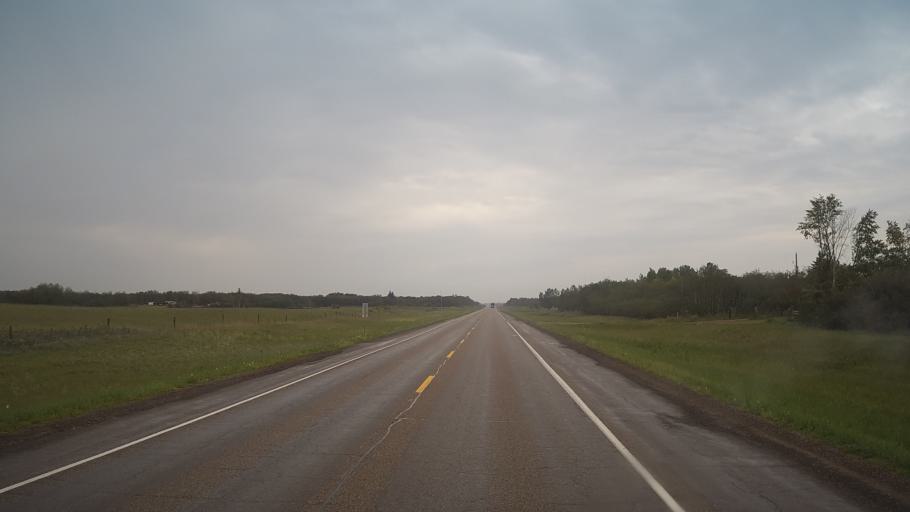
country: CA
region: Saskatchewan
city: Langham
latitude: 52.1293
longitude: -107.0303
